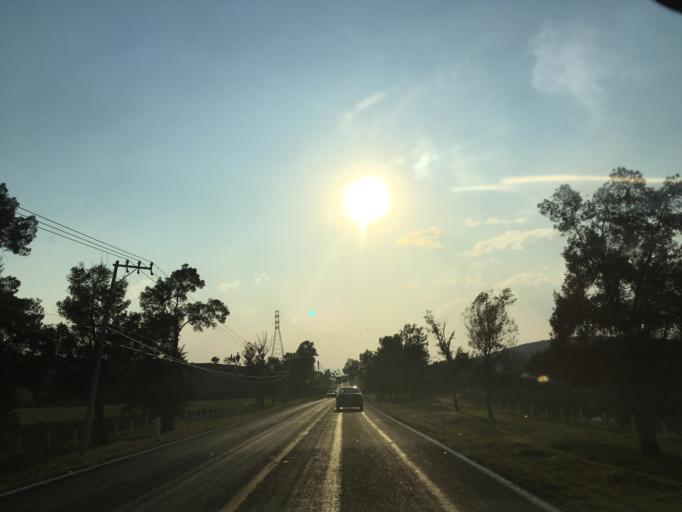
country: MX
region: Michoacan
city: Charo
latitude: 19.7439
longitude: -101.0708
